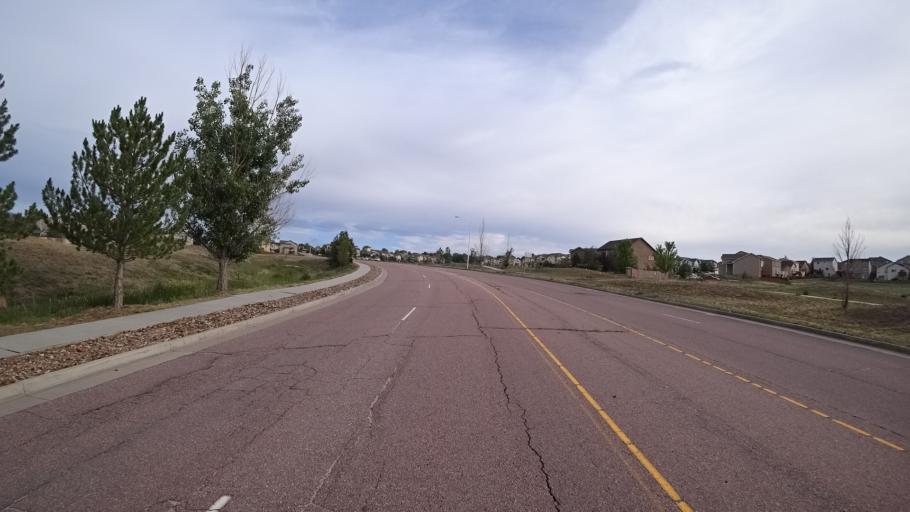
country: US
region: Colorado
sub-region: El Paso County
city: Fountain
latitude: 38.7161
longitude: -104.6863
